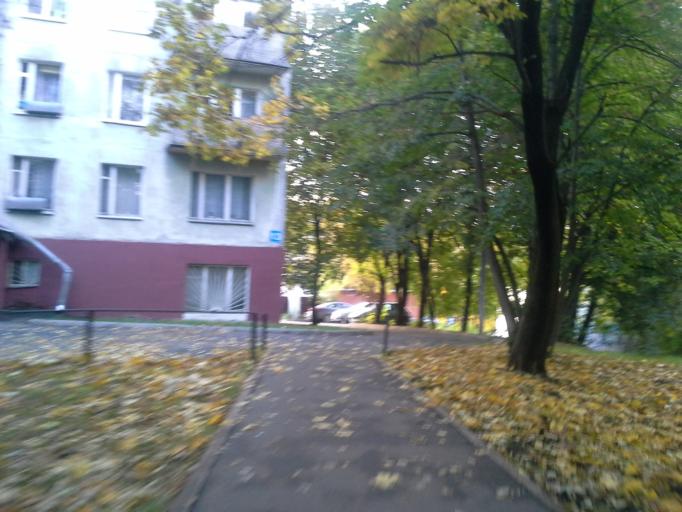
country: RU
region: Moskovskaya
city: Kommunarka
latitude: 55.5278
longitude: 37.4422
